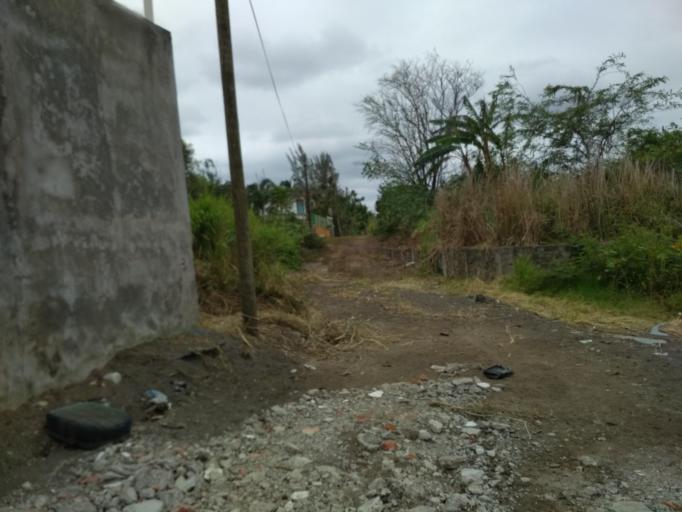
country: MX
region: Veracruz
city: Paso del Toro
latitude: 19.0538
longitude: -96.1347
